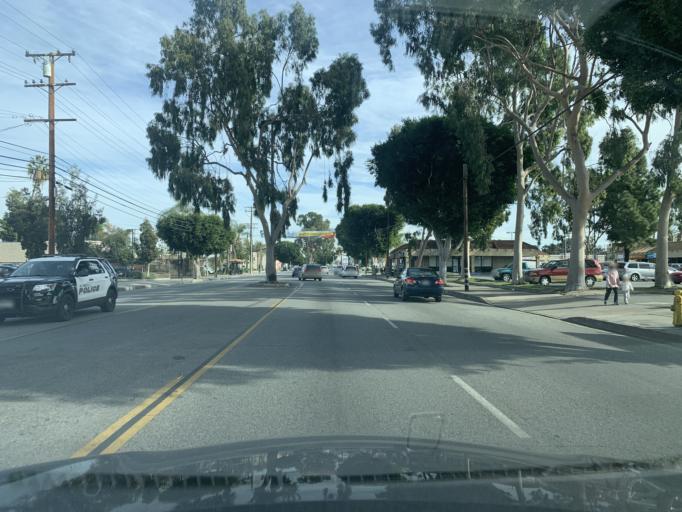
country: US
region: California
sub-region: Los Angeles County
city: South El Monte
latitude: 34.0627
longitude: -118.0441
